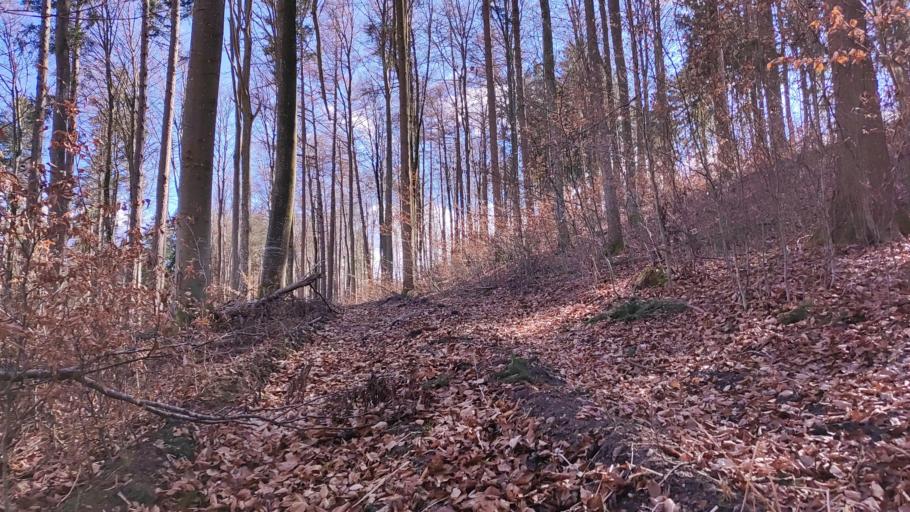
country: DE
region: Bavaria
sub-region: Swabia
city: Zusmarshausen
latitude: 48.4278
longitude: 10.6112
